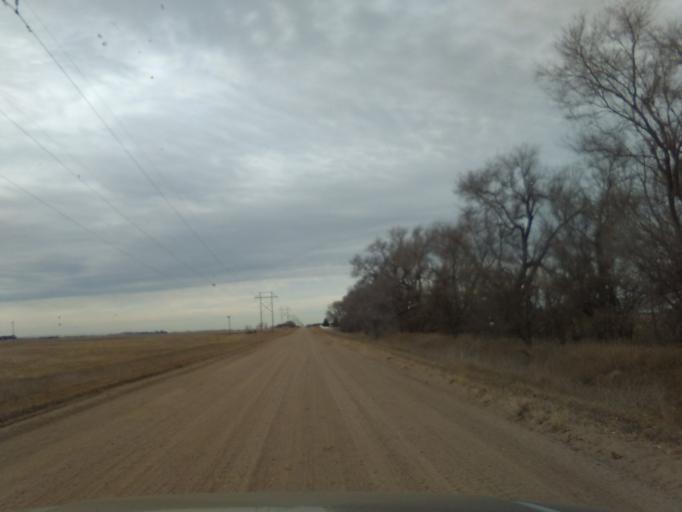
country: US
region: Nebraska
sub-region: Buffalo County
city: Gibbon
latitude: 40.6549
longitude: -98.7596
